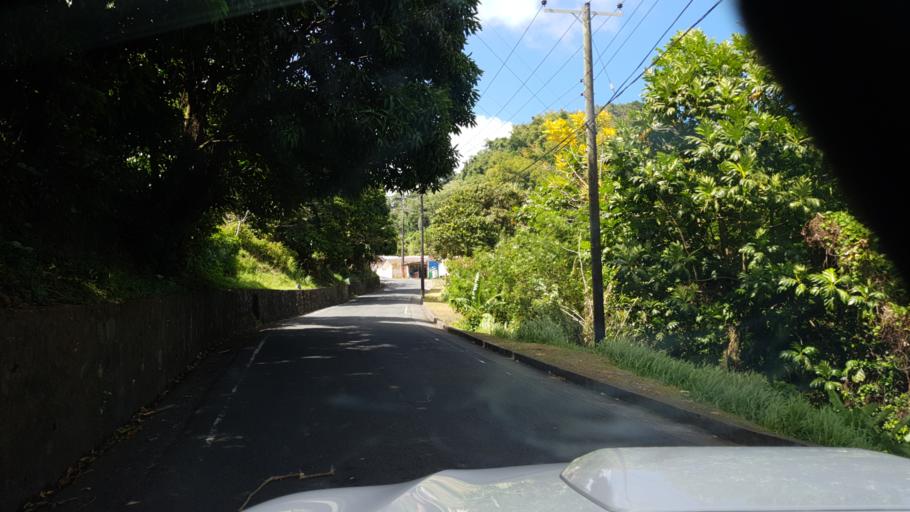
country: LC
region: Castries Quarter
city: Castries
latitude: 13.9873
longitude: -60.9717
